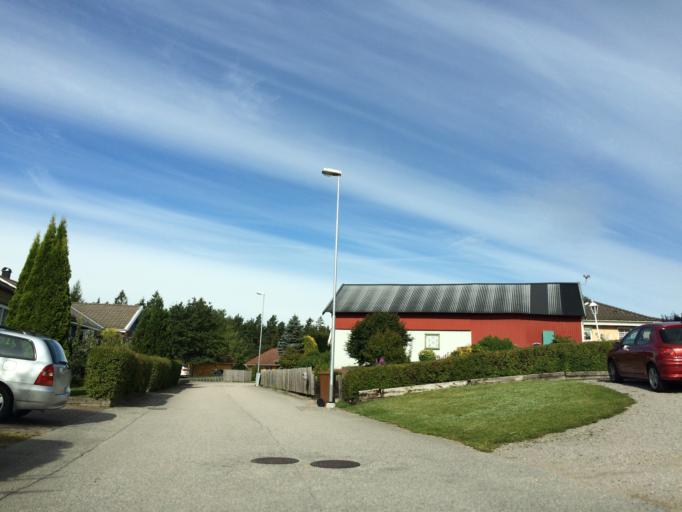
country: SE
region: Vaestra Goetaland
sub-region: Trollhattan
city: Trollhattan
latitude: 58.3236
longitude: 12.2721
